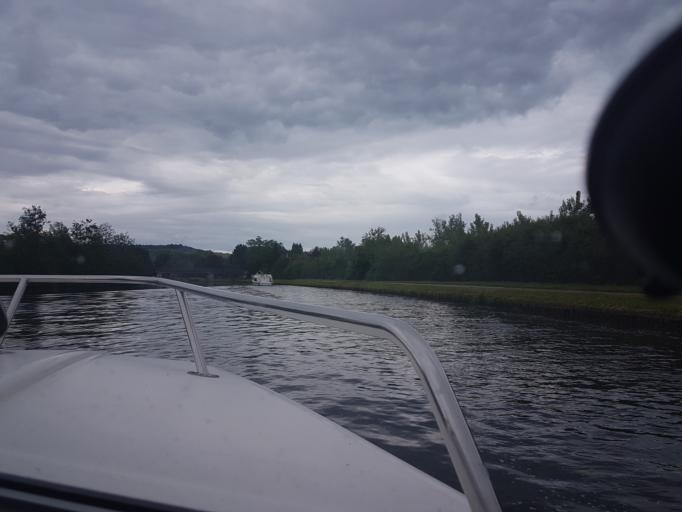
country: FR
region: Bourgogne
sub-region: Departement de l'Yonne
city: Champs-sur-Yonne
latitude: 47.7253
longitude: 3.6106
